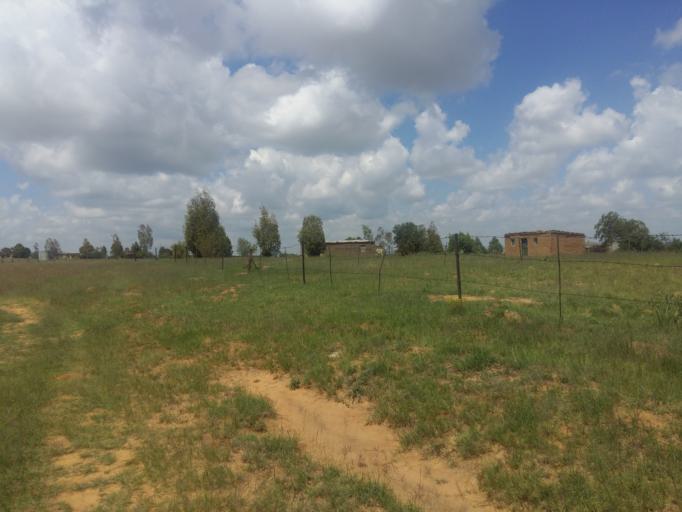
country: LS
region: Mafeteng
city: Mafeteng
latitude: -29.7510
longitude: 27.1139
